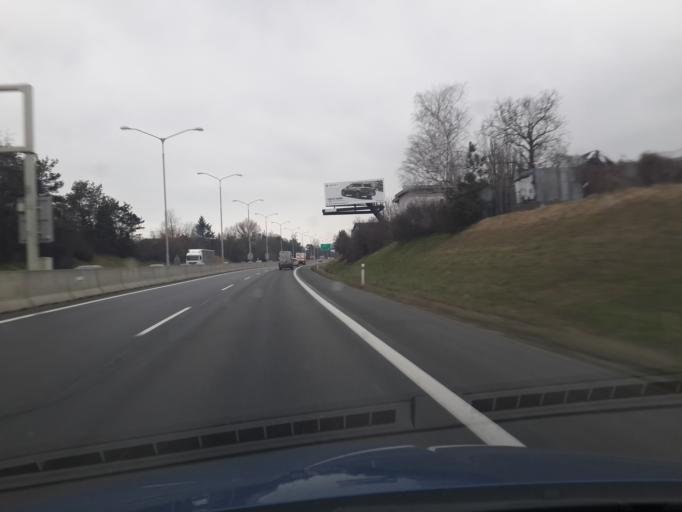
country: AT
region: Lower Austria
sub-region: Politischer Bezirk Bruck an der Leitha
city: Wolfsthal
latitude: 48.1879
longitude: 17.0460
